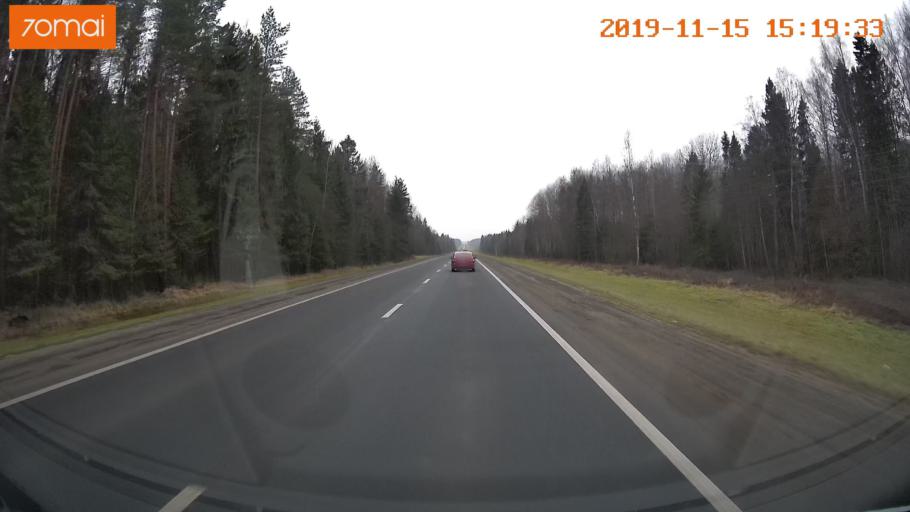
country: RU
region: Jaroslavl
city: Danilov
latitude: 58.2331
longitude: 40.1758
